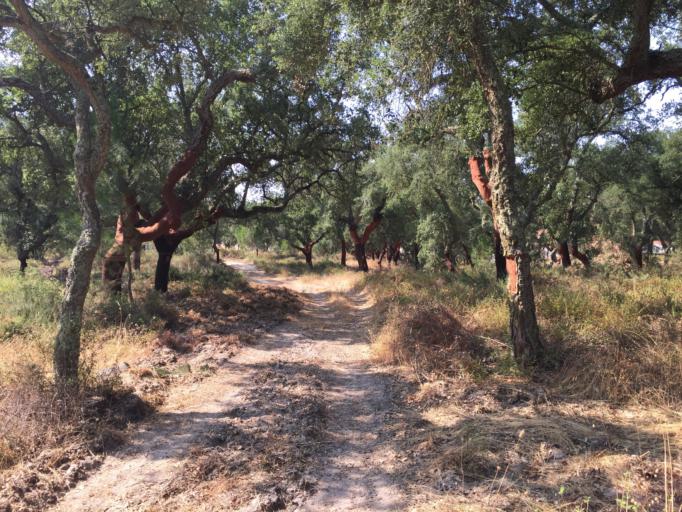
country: PT
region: Setubal
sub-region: Setubal
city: Setubal
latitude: 38.5879
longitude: -8.6879
